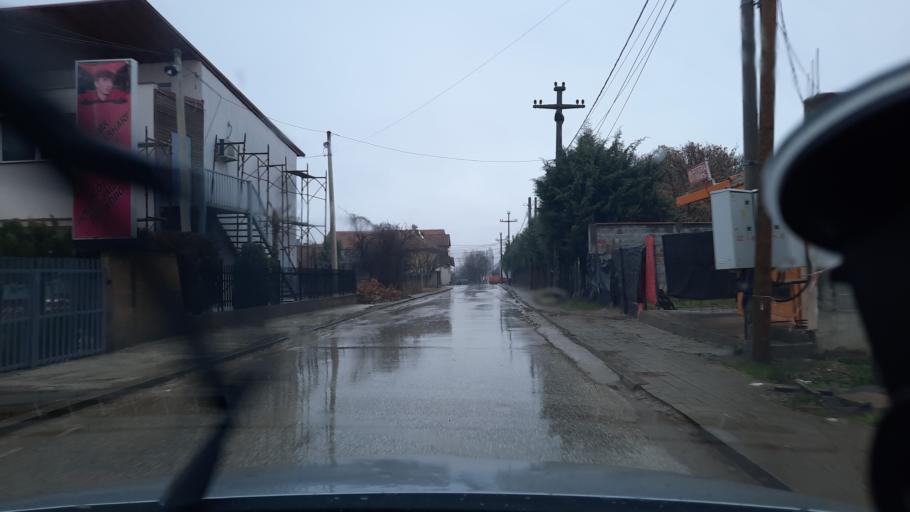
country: MK
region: Opstina Lipkovo
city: Lipkovo
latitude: 42.1523
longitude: 21.5911
